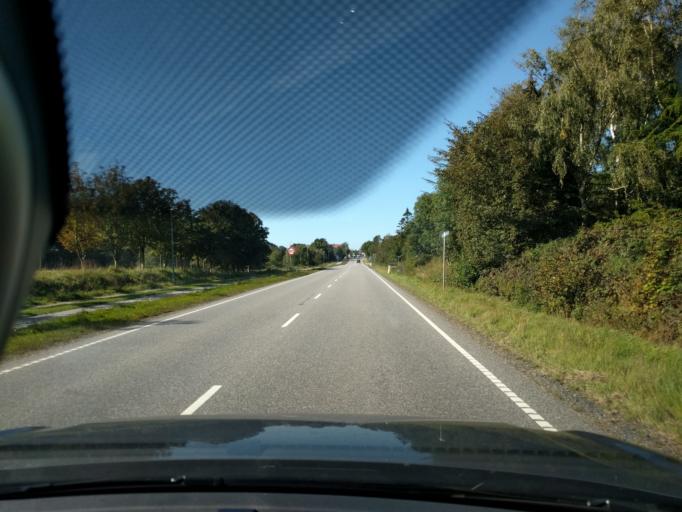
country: DK
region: North Denmark
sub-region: Vesthimmerland Kommune
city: Alestrup
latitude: 56.7045
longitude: 9.6376
